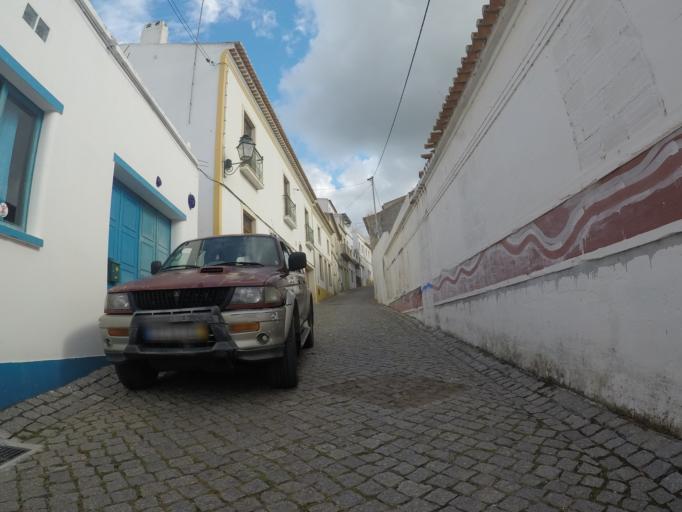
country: PT
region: Faro
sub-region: Aljezur
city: Aljezur
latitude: 37.3181
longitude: -8.8033
